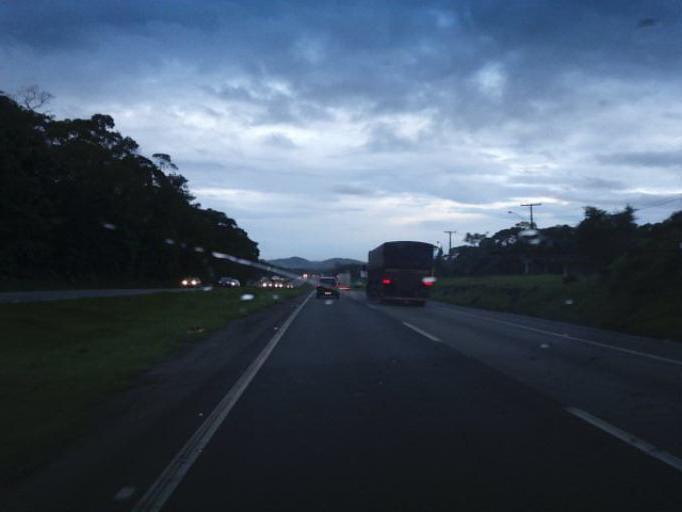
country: BR
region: Santa Catarina
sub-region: Joinville
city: Joinville
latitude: -26.0242
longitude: -48.8617
